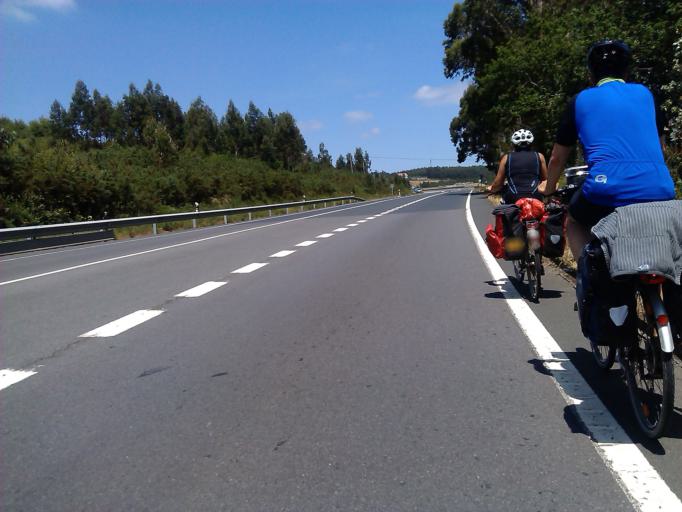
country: ES
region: Galicia
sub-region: Provincia da Coruna
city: Oroso
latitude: 42.9093
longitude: -8.4058
